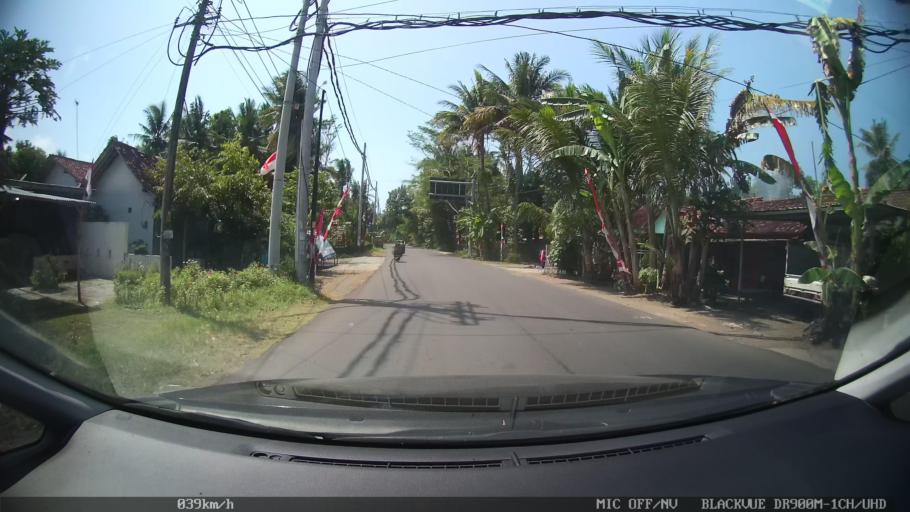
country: ID
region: Daerah Istimewa Yogyakarta
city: Srandakan
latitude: -7.9002
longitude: 110.0672
